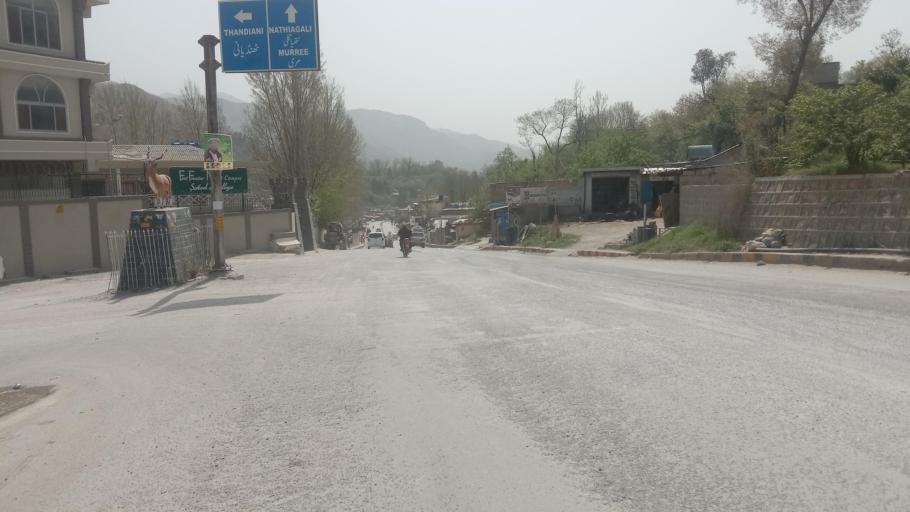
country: PK
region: Khyber Pakhtunkhwa
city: Abbottabad
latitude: 34.1563
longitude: 73.2661
